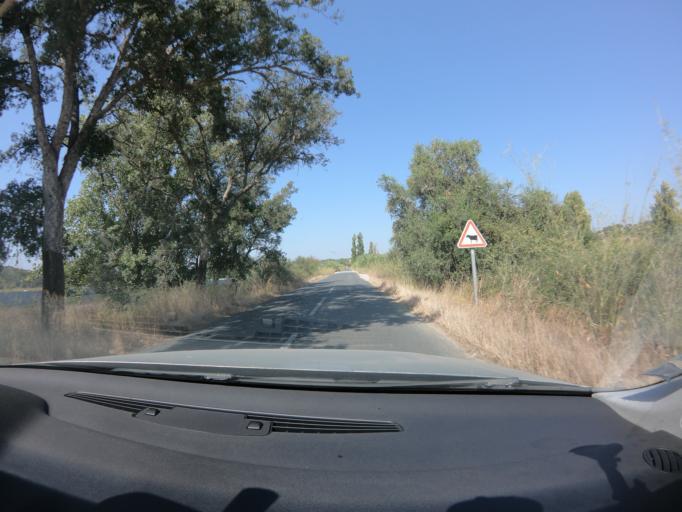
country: PT
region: Setubal
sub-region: Alcacer do Sal
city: Alcacer do Sal
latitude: 38.2841
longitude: -8.4009
